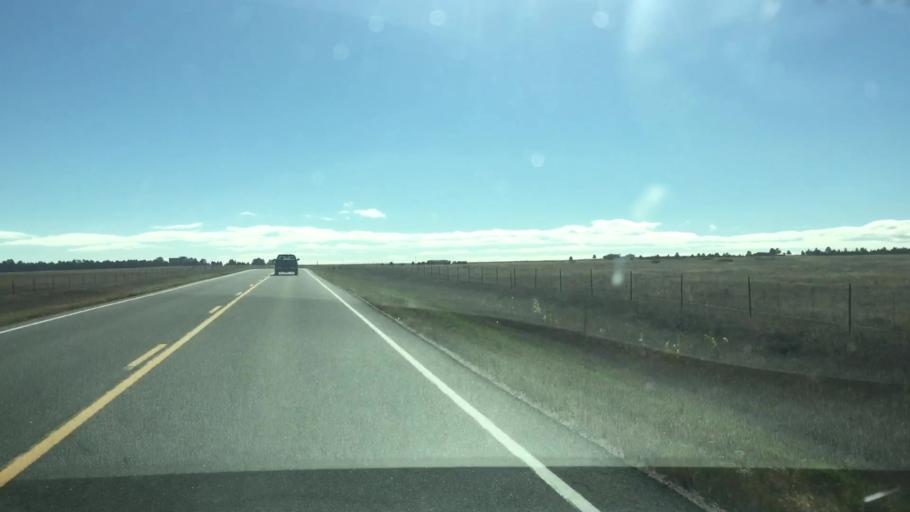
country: US
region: Colorado
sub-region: Elbert County
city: Kiowa
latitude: 39.3373
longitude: -104.4291
